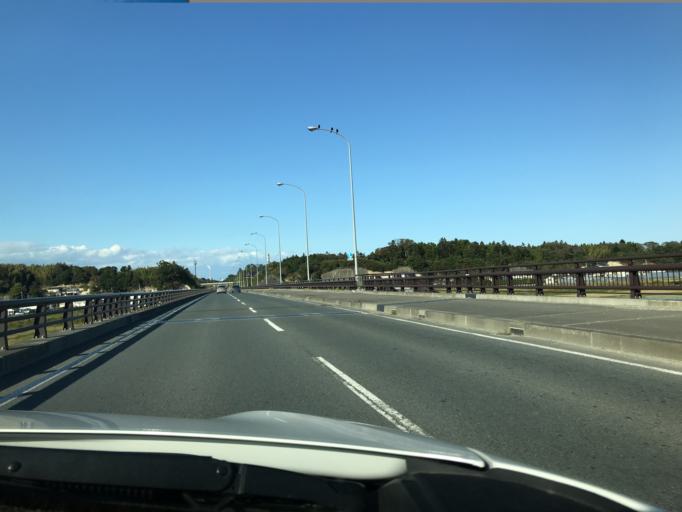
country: JP
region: Miyagi
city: Marumori
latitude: 37.8045
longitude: 140.9436
